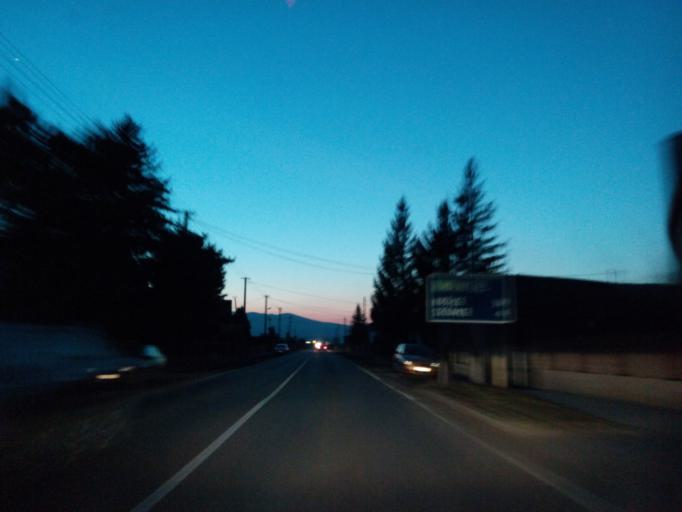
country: SK
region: Kosicky
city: Secovce
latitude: 48.6998
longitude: 21.7057
